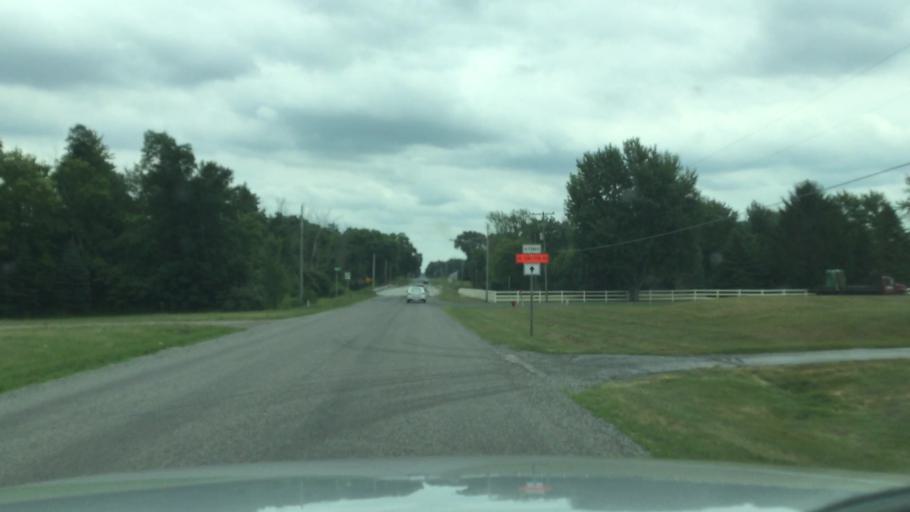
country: US
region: Michigan
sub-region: Saginaw County
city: Frankenmuth
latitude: 43.3217
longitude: -83.7968
